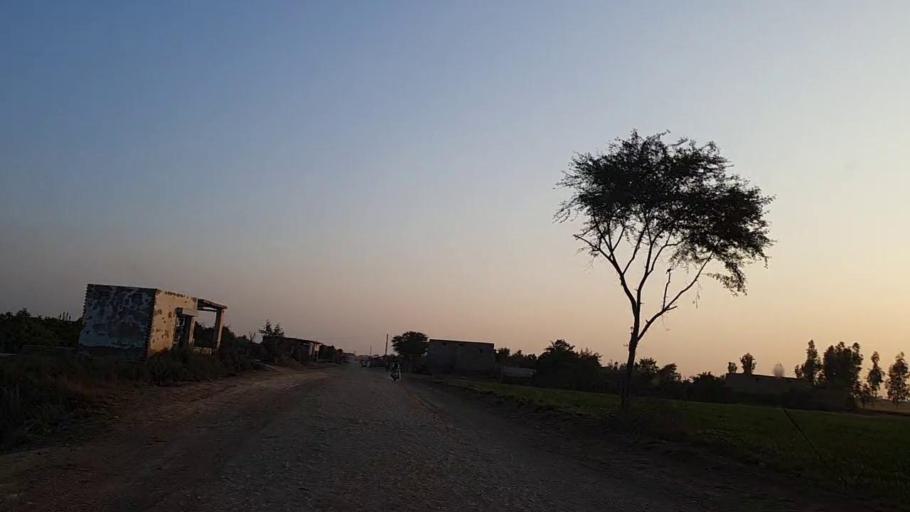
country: PK
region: Sindh
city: Shahdadpur
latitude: 25.9215
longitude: 68.5068
